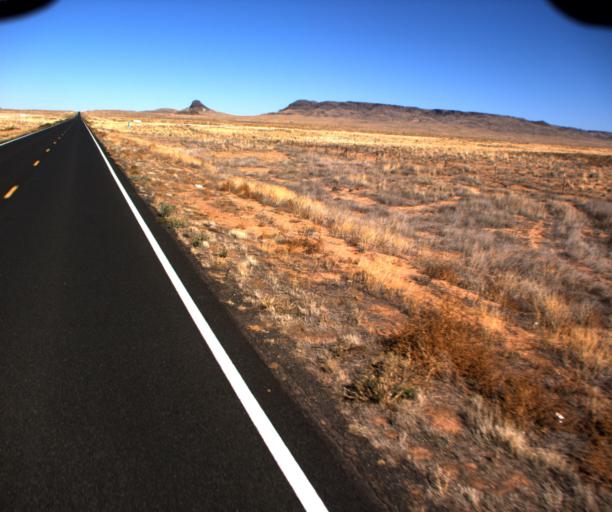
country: US
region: Arizona
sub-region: Navajo County
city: Dilkon
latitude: 35.3728
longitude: -110.4251
